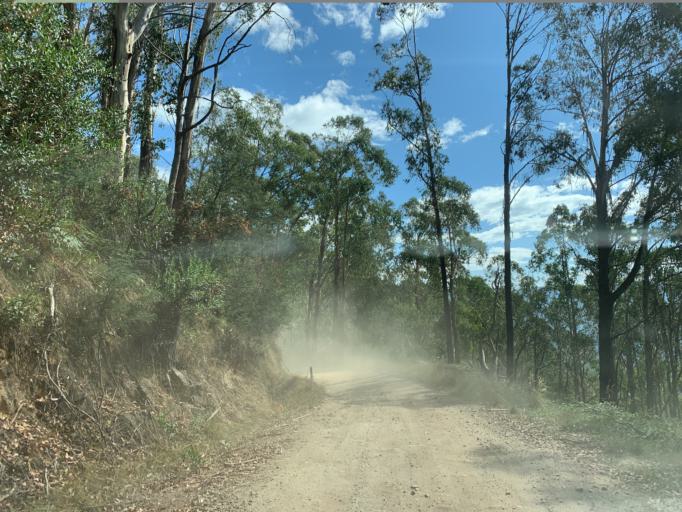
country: AU
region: Victoria
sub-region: Mansfield
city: Mansfield
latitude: -37.0924
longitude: 146.5412
